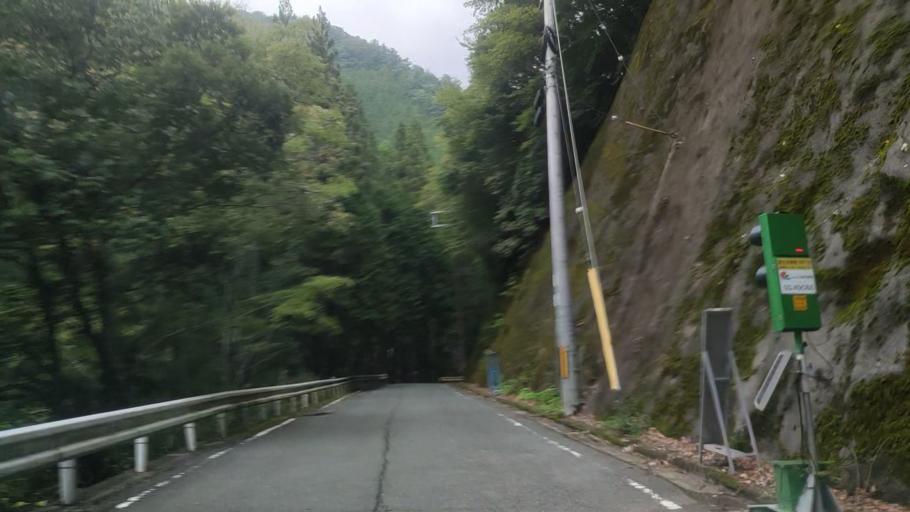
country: JP
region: Wakayama
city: Koya
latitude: 34.2318
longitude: 135.6435
